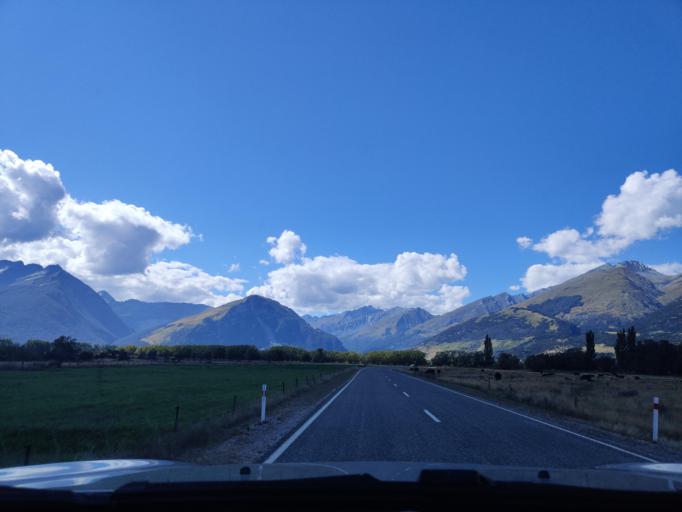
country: NZ
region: Otago
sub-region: Queenstown-Lakes District
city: Queenstown
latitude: -44.7852
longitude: 168.3909
